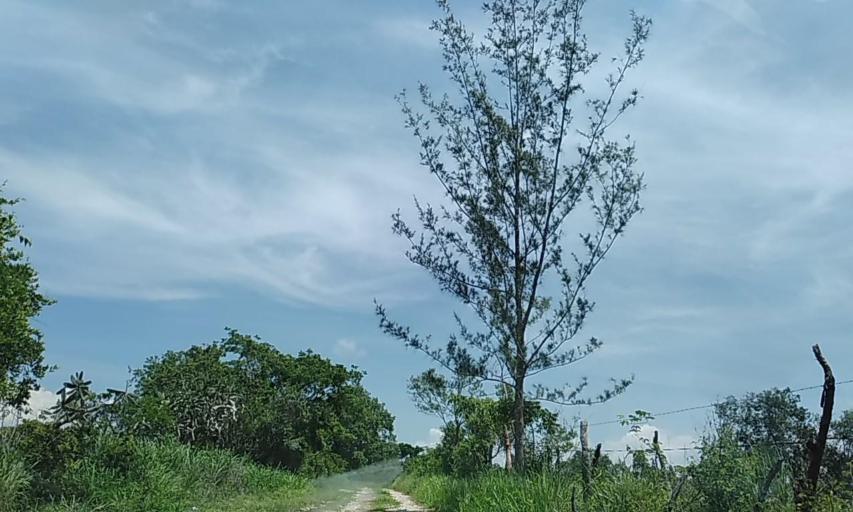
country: MX
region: Veracruz
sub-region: Emiliano Zapata
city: Dos Rios
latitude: 19.4415
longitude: -96.7594
